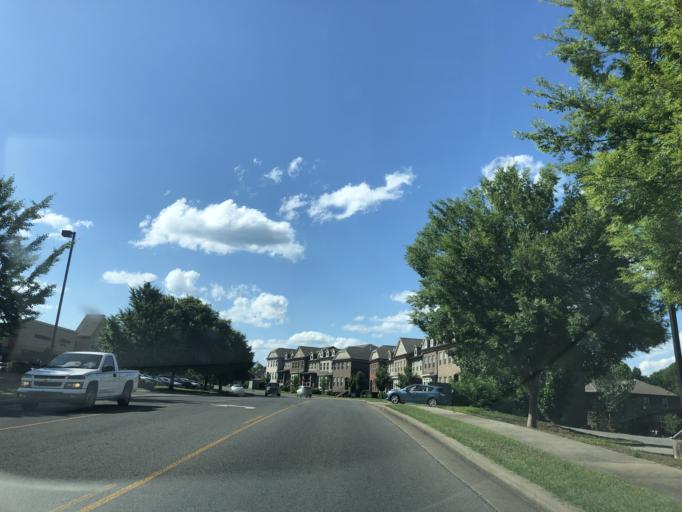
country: US
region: Tennessee
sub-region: Davidson County
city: Belle Meade
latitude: 36.0467
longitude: -86.9508
